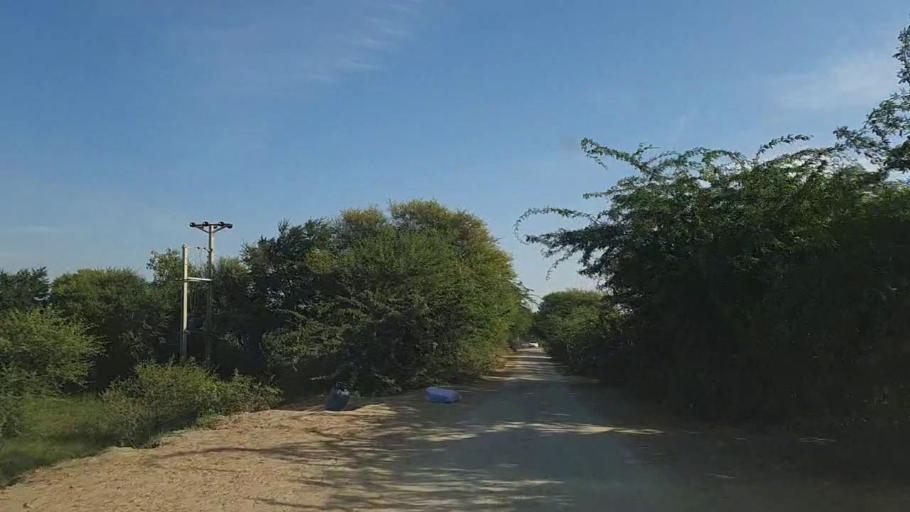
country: PK
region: Sindh
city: Bulri
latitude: 24.7943
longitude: 68.3415
